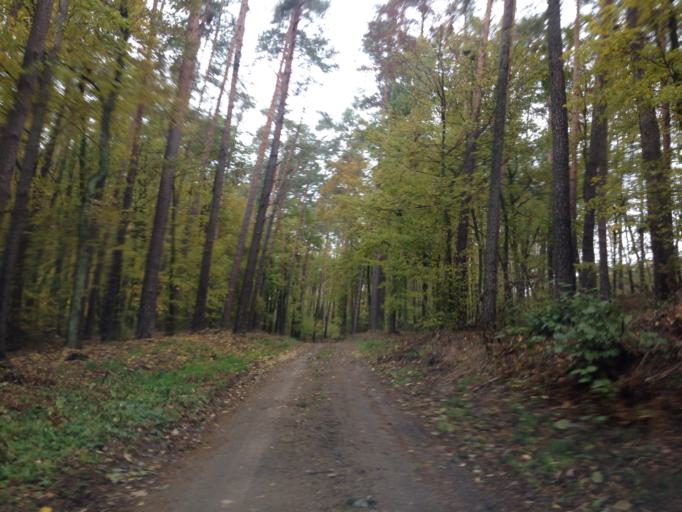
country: PL
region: Kujawsko-Pomorskie
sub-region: Powiat brodnicki
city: Gorzno
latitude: 53.2555
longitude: 19.6897
